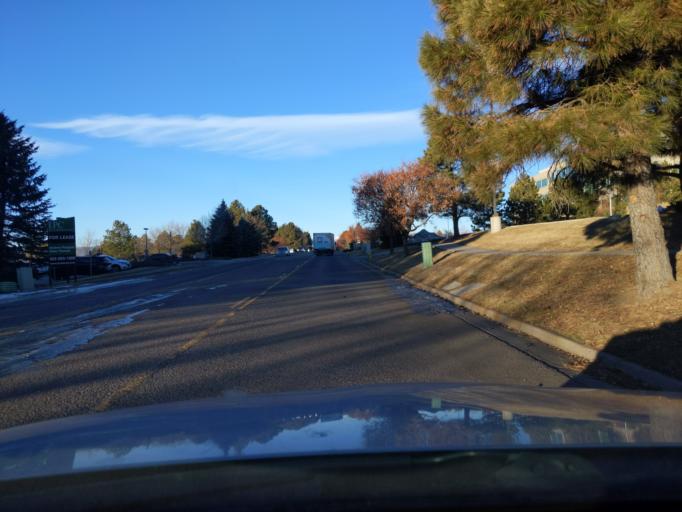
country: US
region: Colorado
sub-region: Arapahoe County
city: Centennial
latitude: 39.5720
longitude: -104.8808
